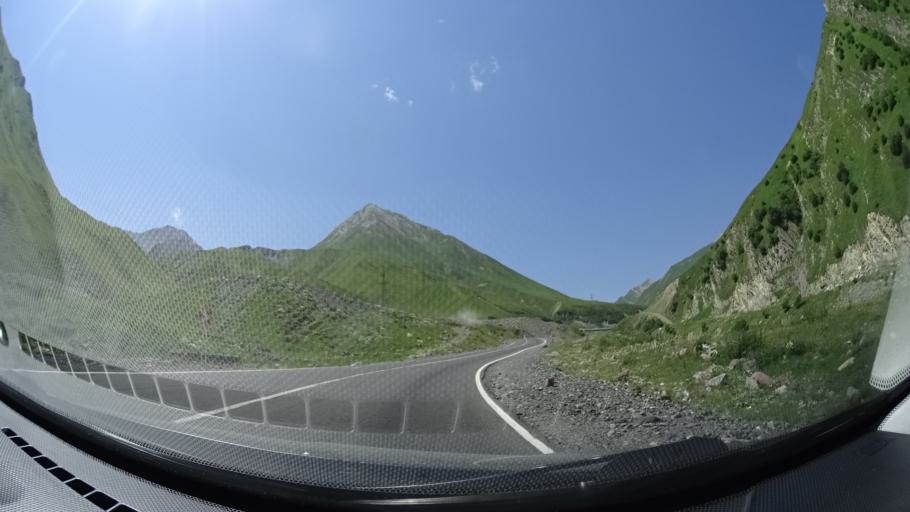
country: GE
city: Gudauri
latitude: 42.5447
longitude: 44.4918
